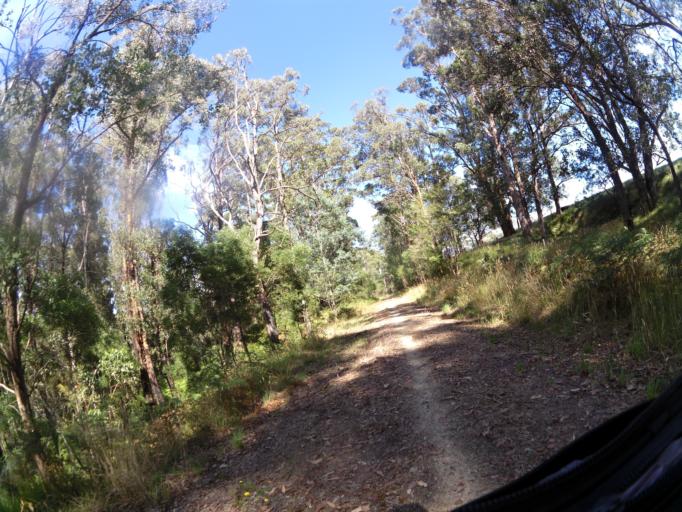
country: AU
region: Victoria
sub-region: East Gippsland
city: Lakes Entrance
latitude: -37.7504
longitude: 148.1855
